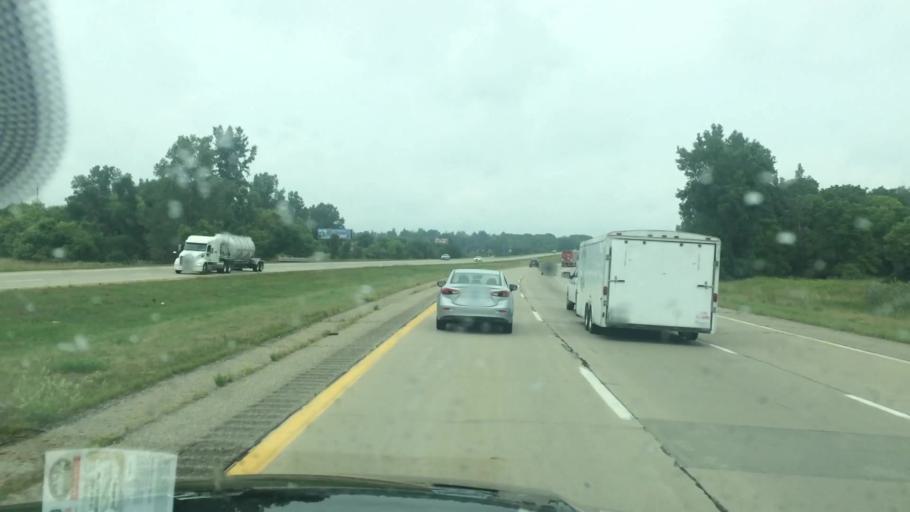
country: US
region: Michigan
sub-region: Eaton County
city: Charlotte
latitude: 42.5692
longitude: -84.8208
